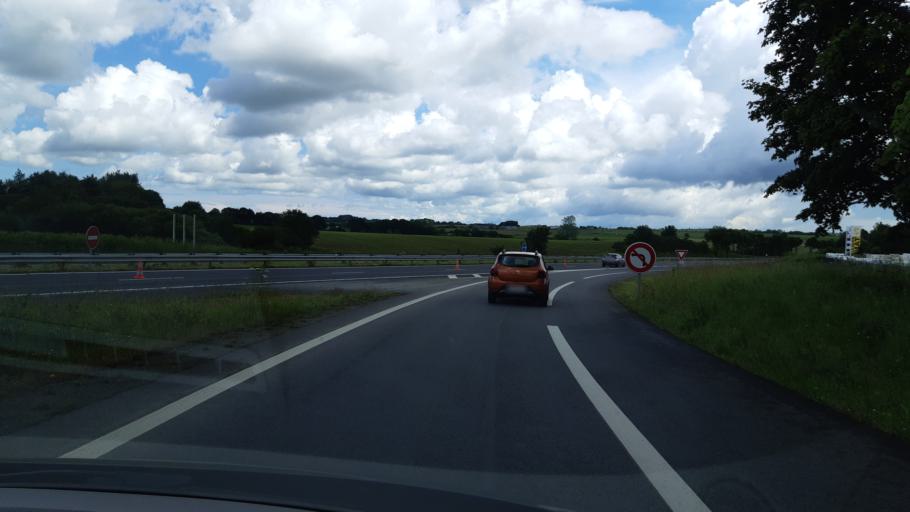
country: FR
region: Brittany
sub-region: Departement du Finistere
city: Landivisiau
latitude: 48.5180
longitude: -4.0520
